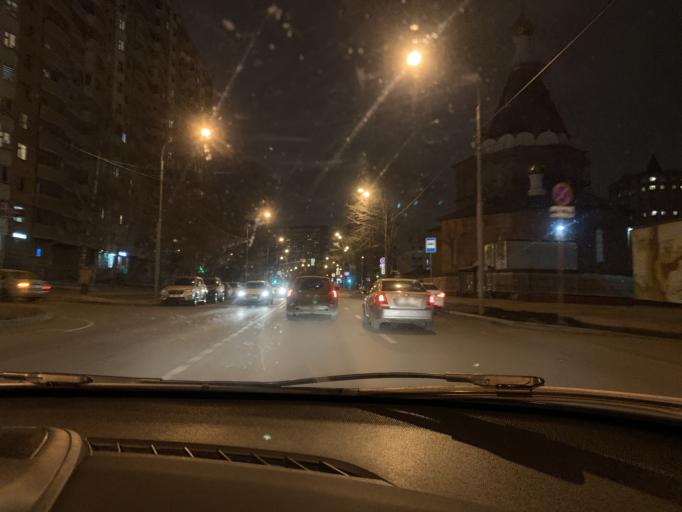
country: RU
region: Moskovskaya
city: Vostochnoe Degunino
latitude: 55.8724
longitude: 37.5595
